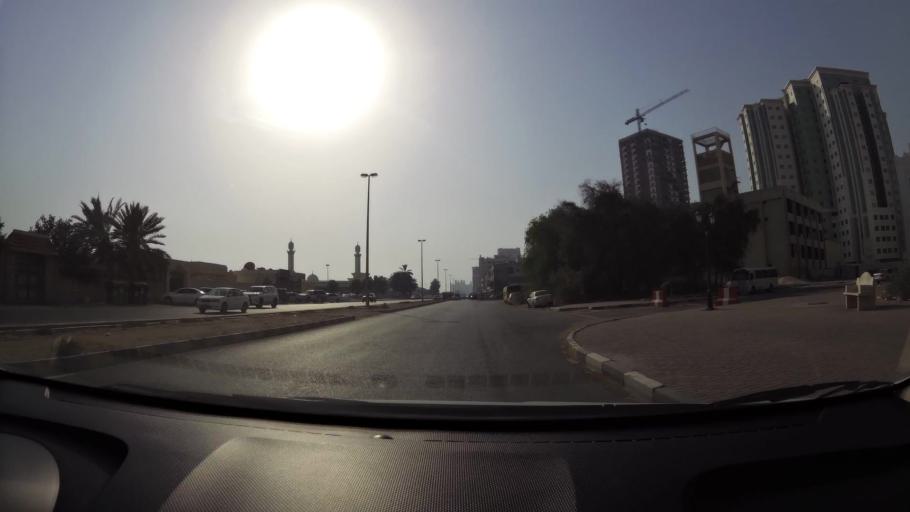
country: AE
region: Ajman
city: Ajman
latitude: 25.3878
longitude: 55.4374
